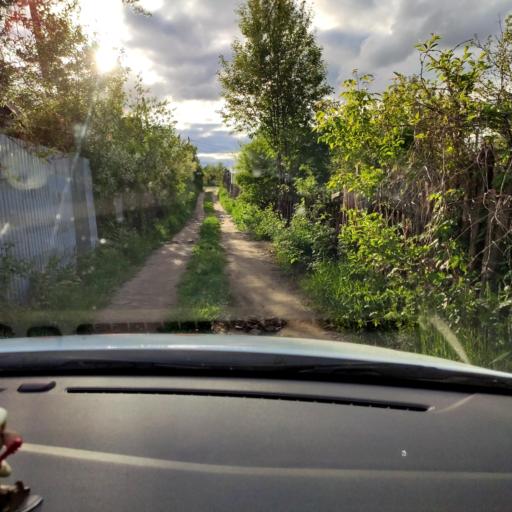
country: RU
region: Tatarstan
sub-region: Gorod Kazan'
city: Kazan
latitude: 55.8447
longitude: 49.1924
